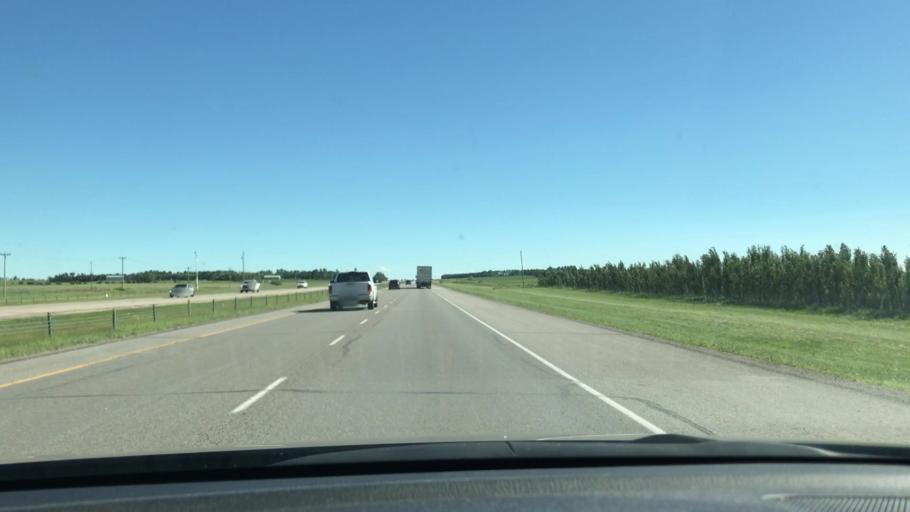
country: CA
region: Alberta
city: Olds
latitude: 51.8997
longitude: -114.0254
